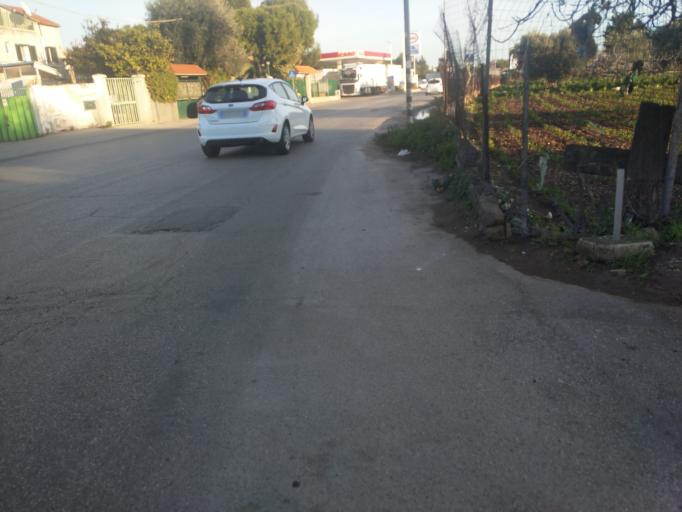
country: IT
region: Apulia
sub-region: Provincia di Bari
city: Bari
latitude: 41.1146
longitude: 16.8412
